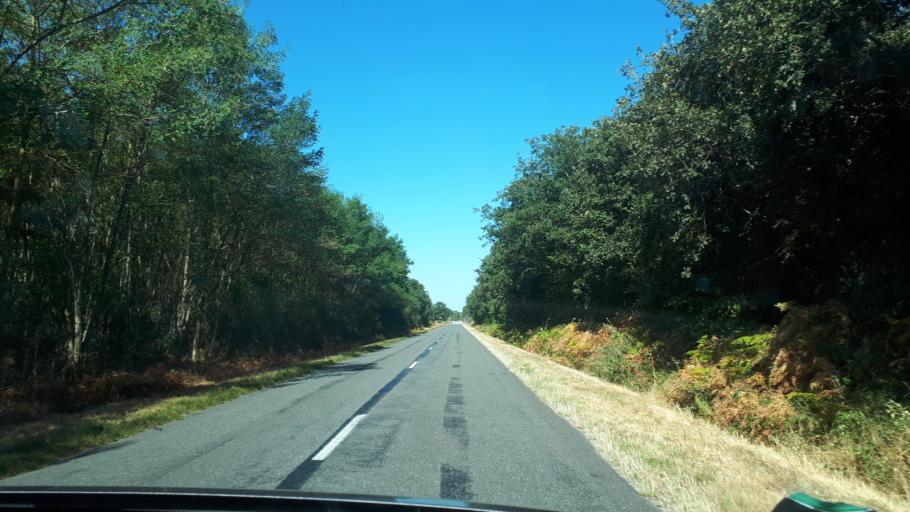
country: FR
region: Centre
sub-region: Departement du Loiret
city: Coullons
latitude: 47.6356
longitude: 2.4526
